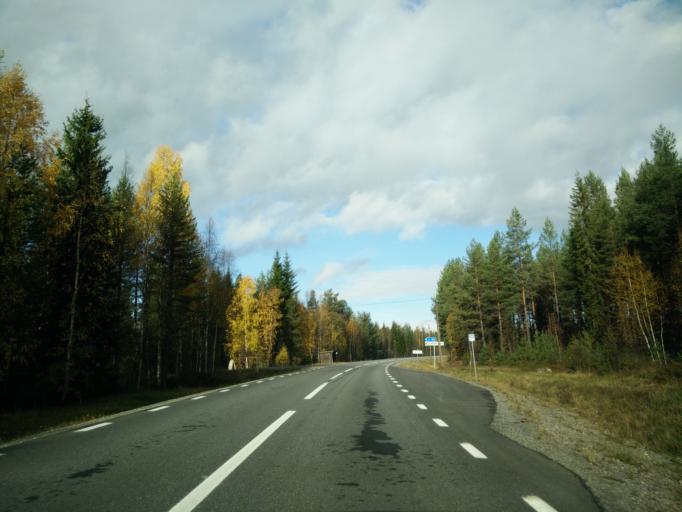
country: SE
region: Jaemtland
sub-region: Braecke Kommun
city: Braecke
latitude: 62.4199
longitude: 15.0018
